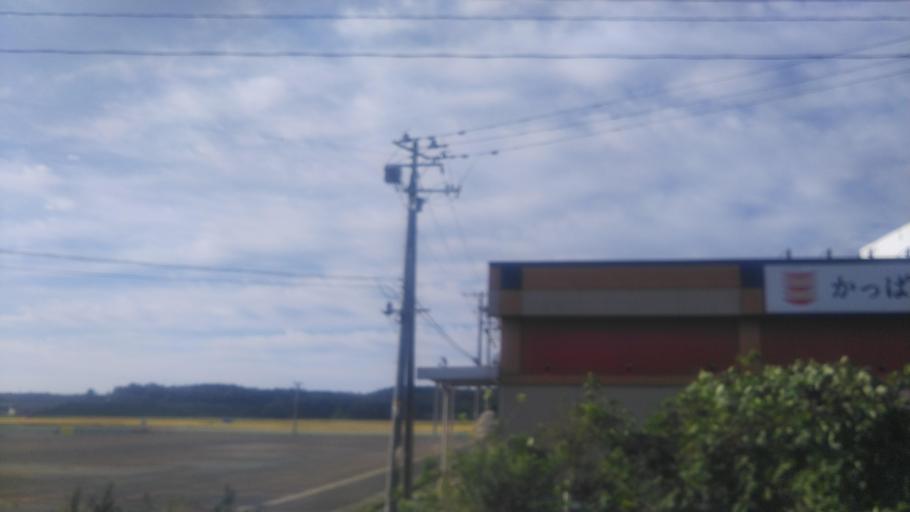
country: JP
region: Akita
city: Noshiromachi
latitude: 40.1843
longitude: 140.0544
